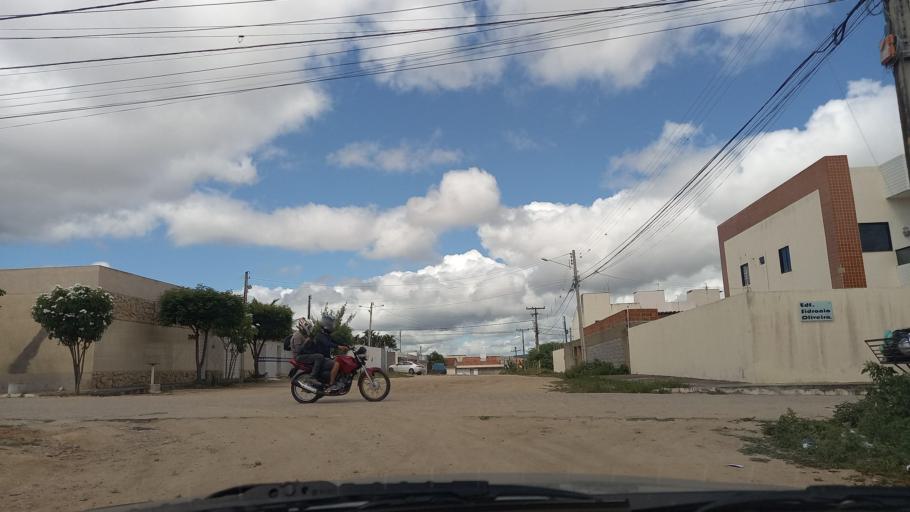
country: BR
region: Pernambuco
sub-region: Caruaru
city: Caruaru
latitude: -8.2568
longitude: -35.9811
